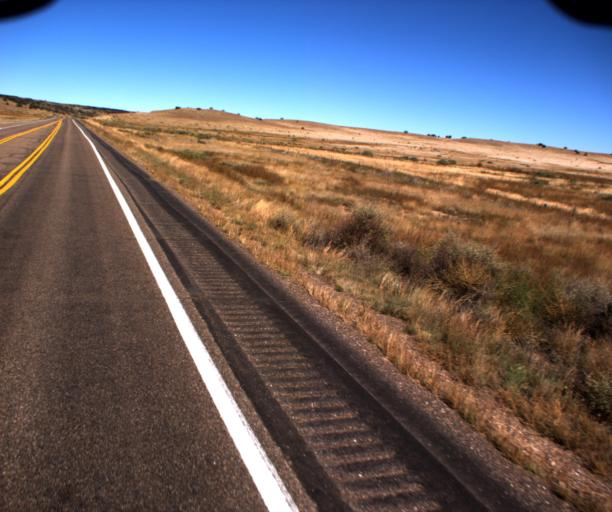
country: US
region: Arizona
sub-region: Apache County
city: Saint Johns
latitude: 34.3227
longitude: -109.3841
